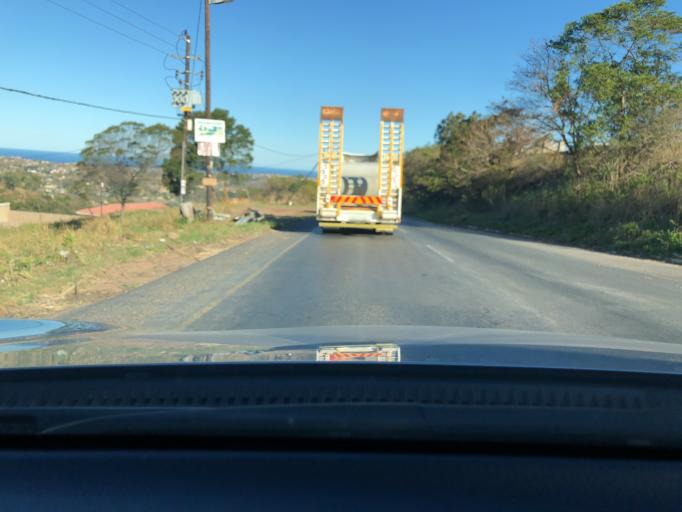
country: ZA
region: KwaZulu-Natal
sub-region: eThekwini Metropolitan Municipality
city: Umkomaas
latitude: -30.0201
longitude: 30.8095
